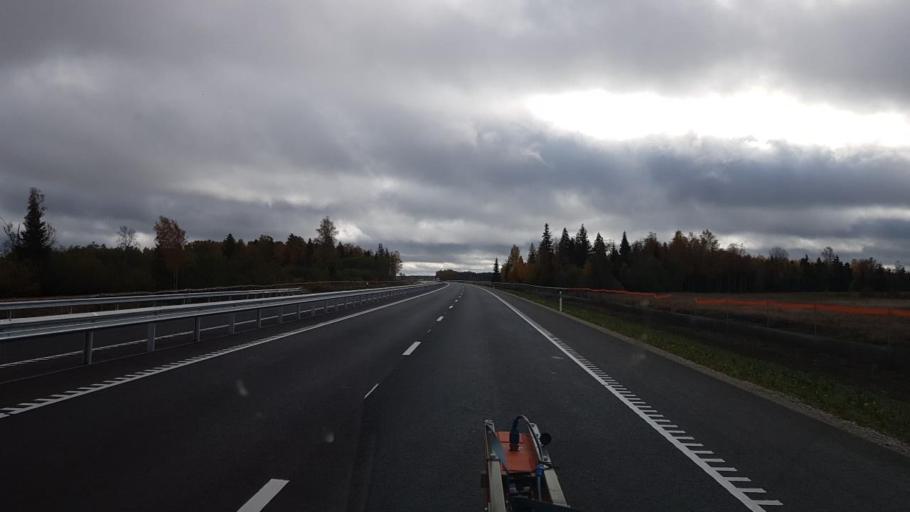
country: EE
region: Jaervamaa
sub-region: Paide linn
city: Paide
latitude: 59.0103
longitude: 25.5597
